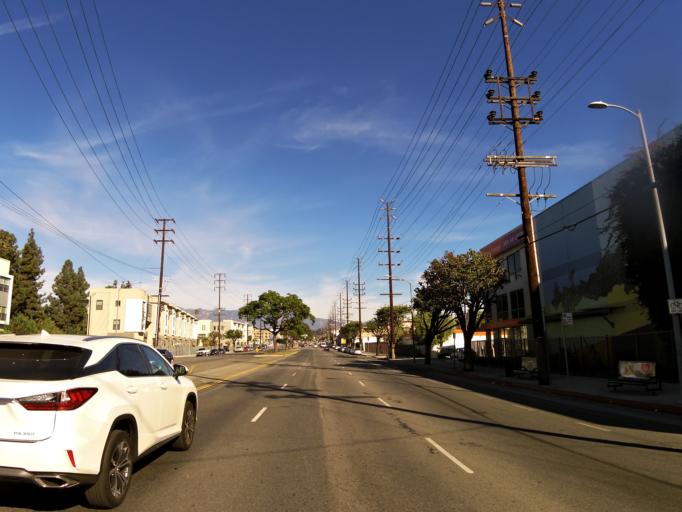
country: US
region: California
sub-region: Los Angeles County
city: Glendale
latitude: 34.1184
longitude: -118.2322
